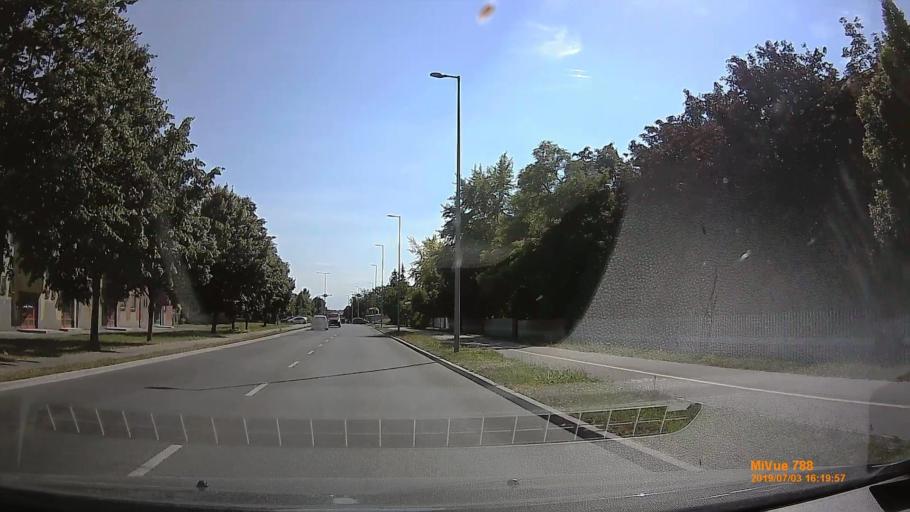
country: HU
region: Gyor-Moson-Sopron
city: Gyor
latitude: 47.6849
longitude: 17.6145
